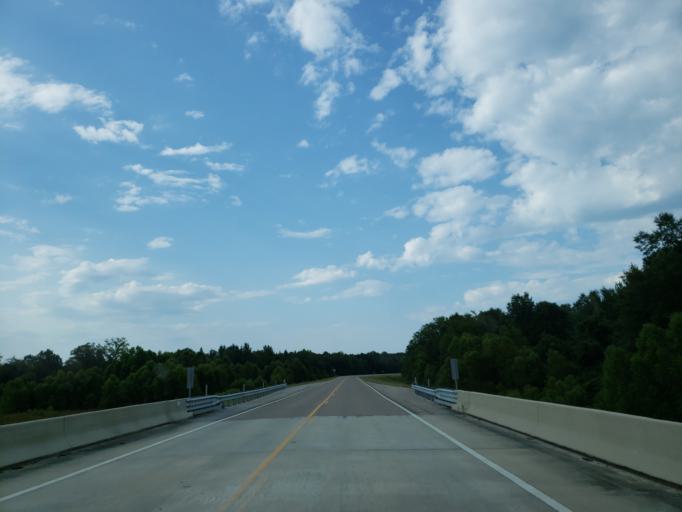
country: US
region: Mississippi
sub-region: Clarke County
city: Stonewall
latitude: 32.1725
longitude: -88.9298
